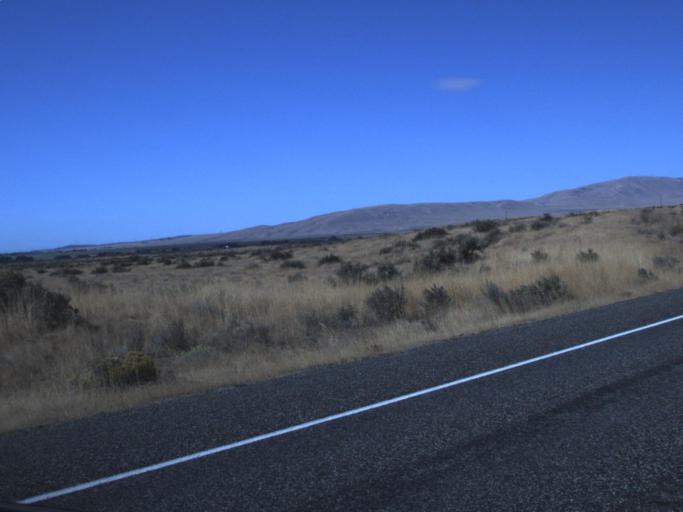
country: US
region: Washington
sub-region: Benton County
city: West Richland
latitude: 46.3369
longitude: -119.3377
